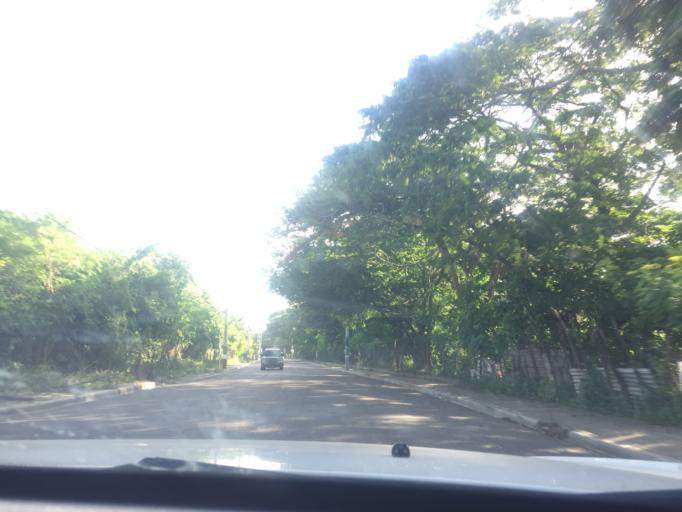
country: DO
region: Santiago
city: Tamboril
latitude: 19.4780
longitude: -70.6406
